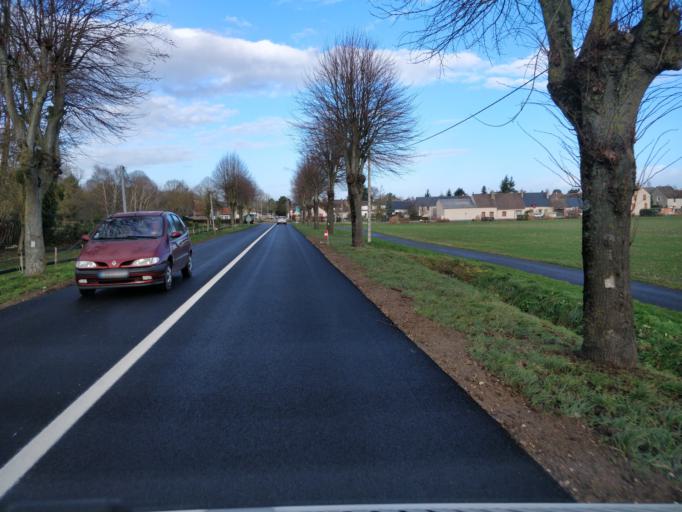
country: FR
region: Centre
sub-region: Departement du Loir-et-Cher
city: Mer
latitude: 47.6908
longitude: 1.5134
